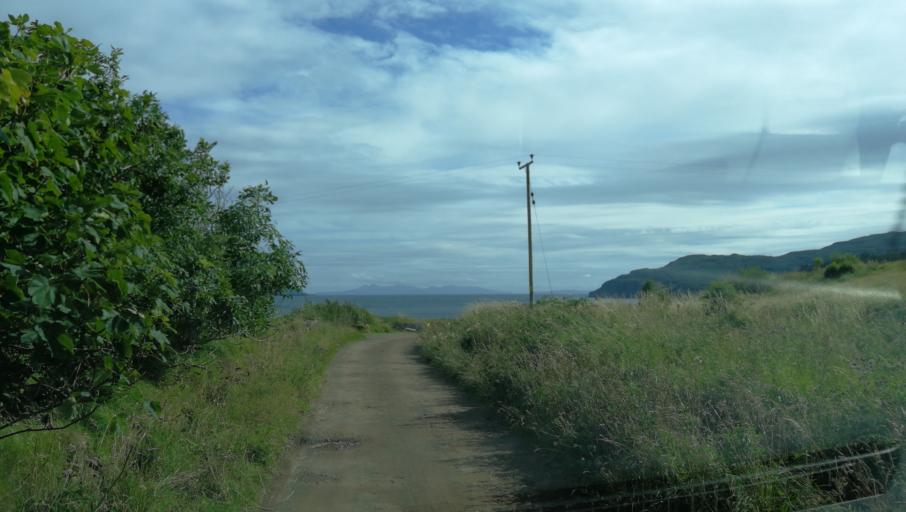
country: GB
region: Scotland
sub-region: Highland
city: Isle of Skye
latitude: 57.3931
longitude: -6.5653
